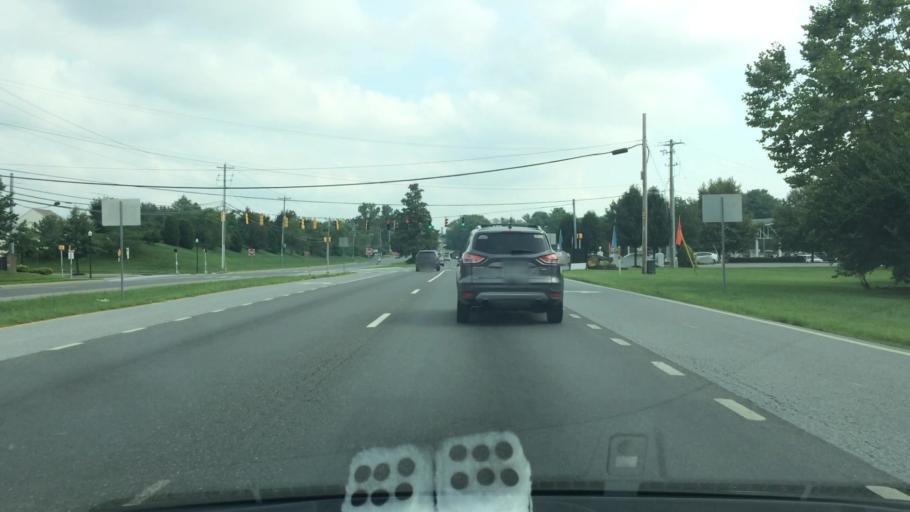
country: US
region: Delaware
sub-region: New Castle County
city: Bear
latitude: 39.6403
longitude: -75.6274
